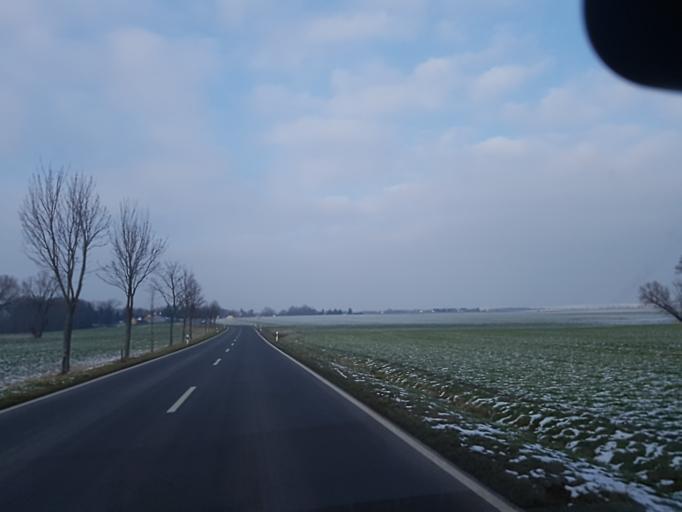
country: DE
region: Saxony
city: Oschatz
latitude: 51.3319
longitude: 13.0936
